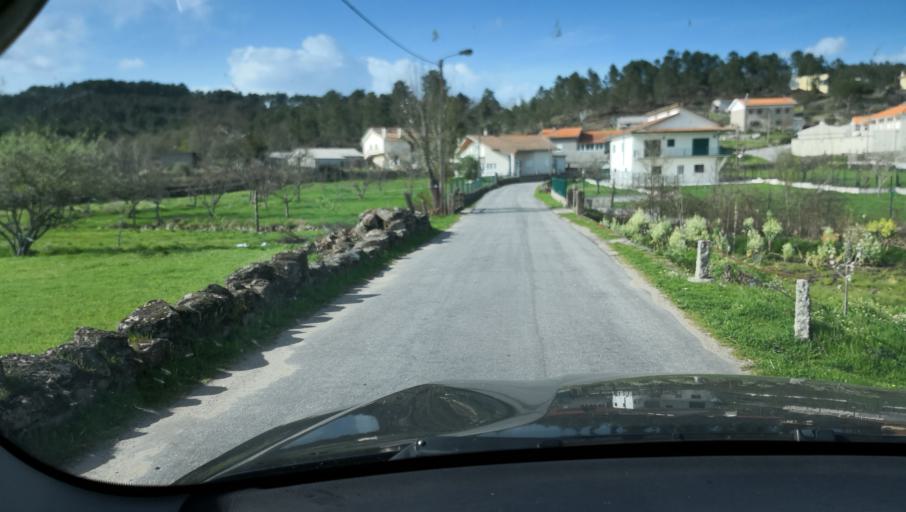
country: PT
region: Vila Real
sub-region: Vila Real
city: Vila Real
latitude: 41.2824
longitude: -7.6689
